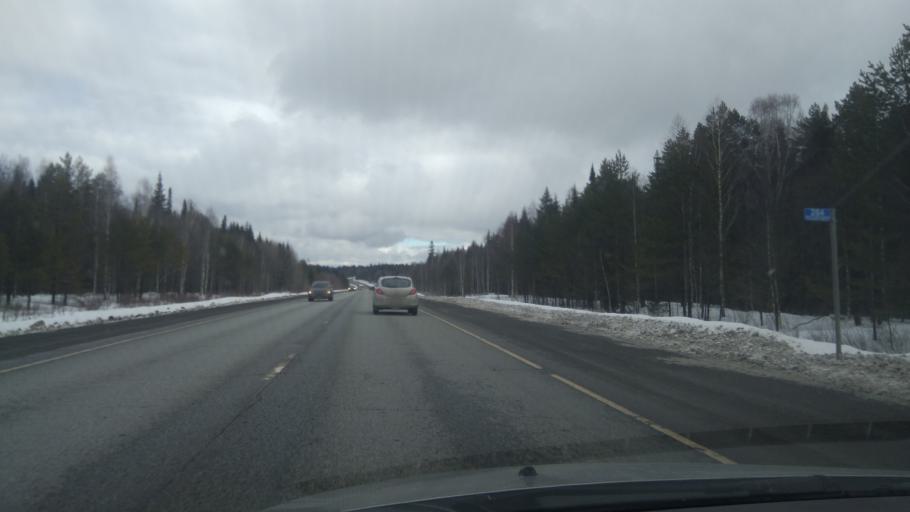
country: RU
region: Sverdlovsk
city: Druzhinino
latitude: 56.7968
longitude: 59.4359
